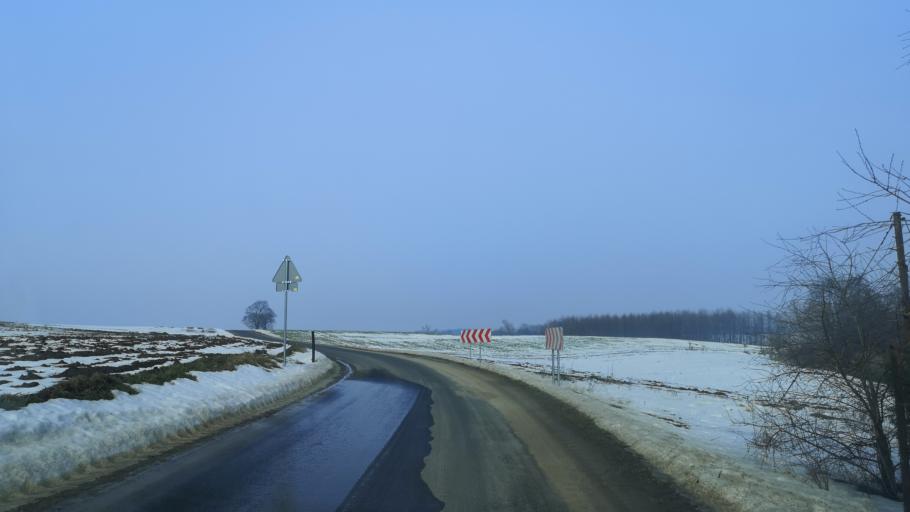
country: PL
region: Warmian-Masurian Voivodeship
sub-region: Powiat nowomiejski
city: Biskupiec
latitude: 53.5301
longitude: 19.3533
